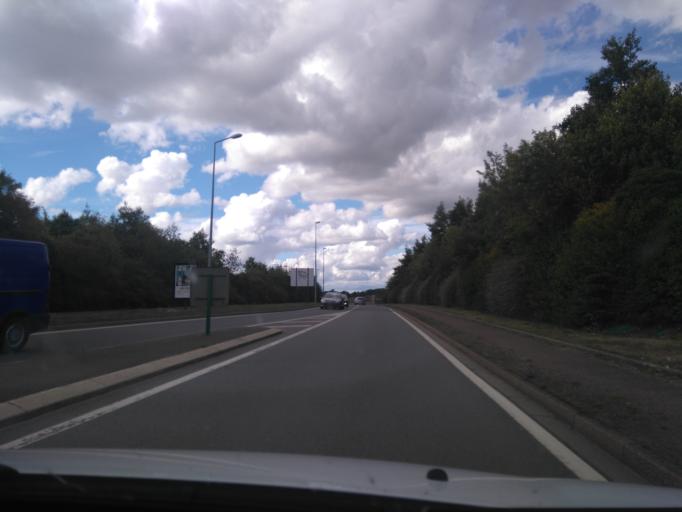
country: FR
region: Brittany
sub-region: Departement d'Ille-et-Vilaine
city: Cesson-Sevigne
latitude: 48.1087
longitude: -1.6165
